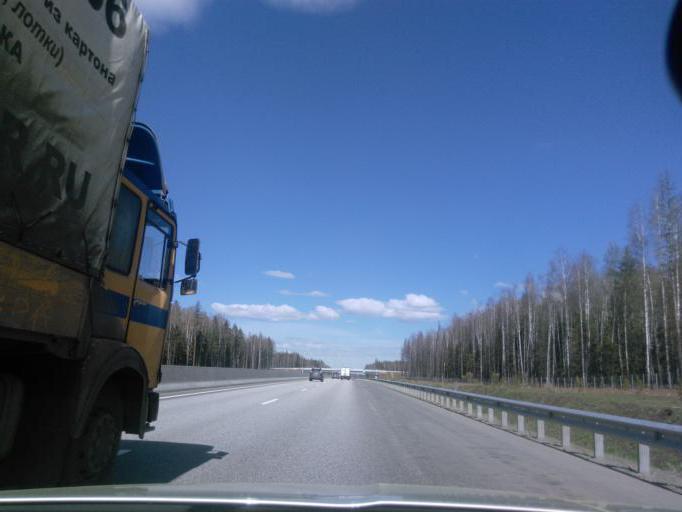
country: RU
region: Moskovskaya
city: Mendeleyevo
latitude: 56.0601
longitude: 37.2424
